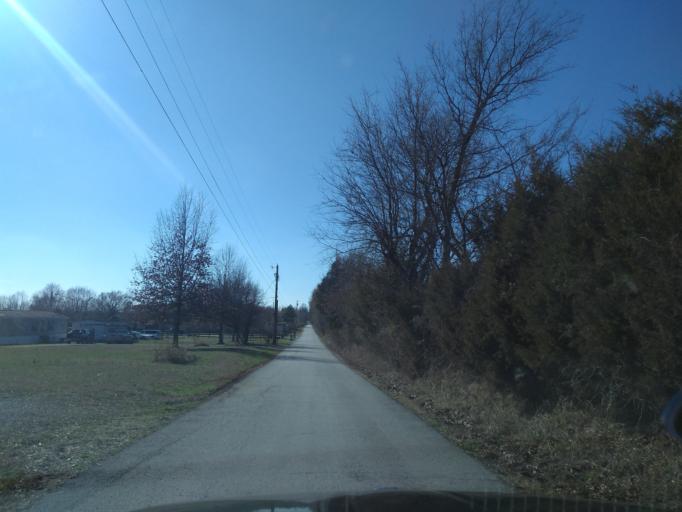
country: US
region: Arkansas
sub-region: Washington County
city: Farmington
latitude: 36.0678
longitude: -94.2420
